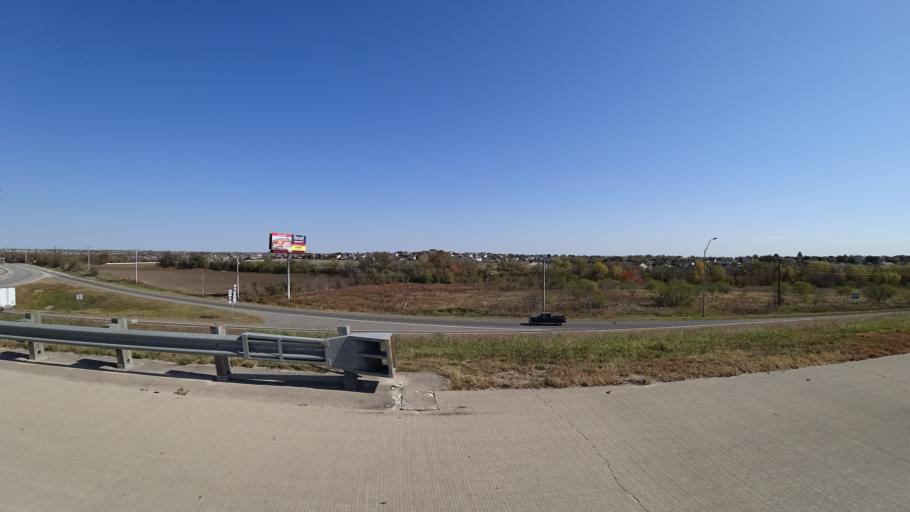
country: US
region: Texas
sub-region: Williamson County
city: Hutto
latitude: 30.5128
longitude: -97.5752
